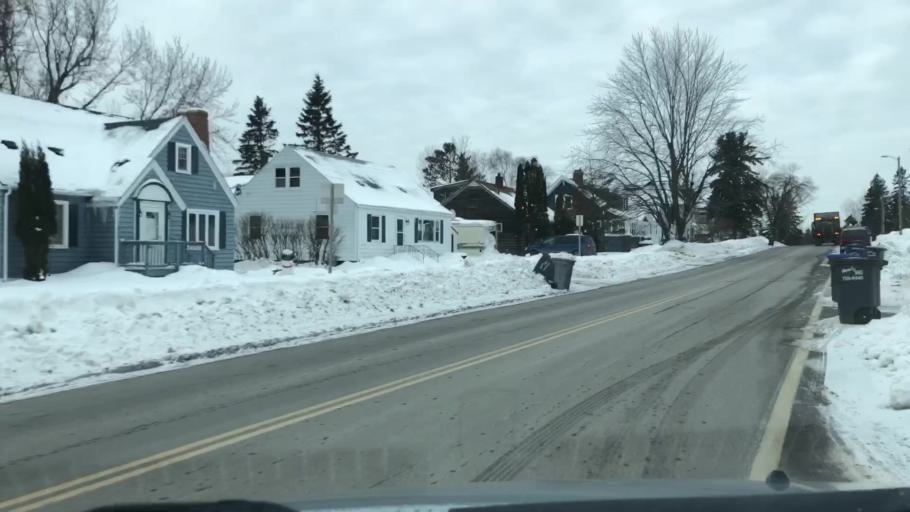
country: US
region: Minnesota
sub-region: Saint Louis County
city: Arnold
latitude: 46.8339
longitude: -92.0639
